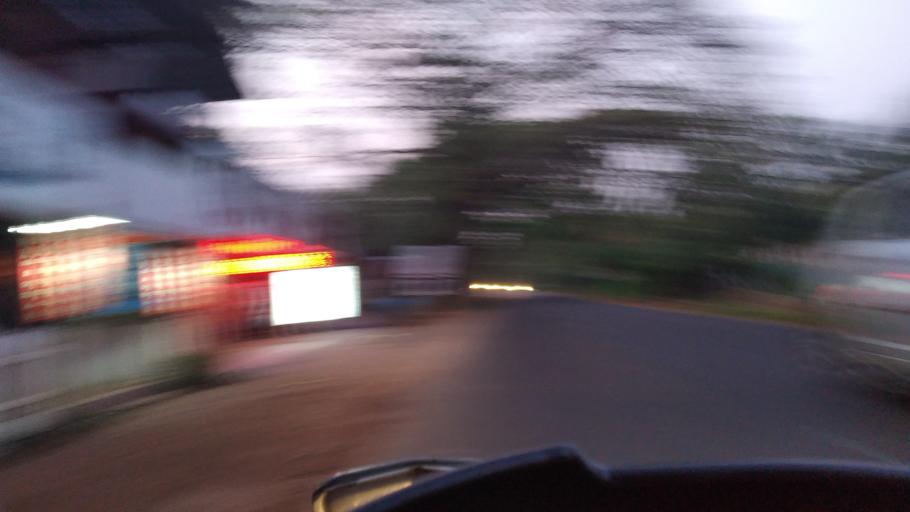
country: IN
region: Kerala
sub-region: Kottayam
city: Kottayam
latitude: 9.6165
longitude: 76.4323
